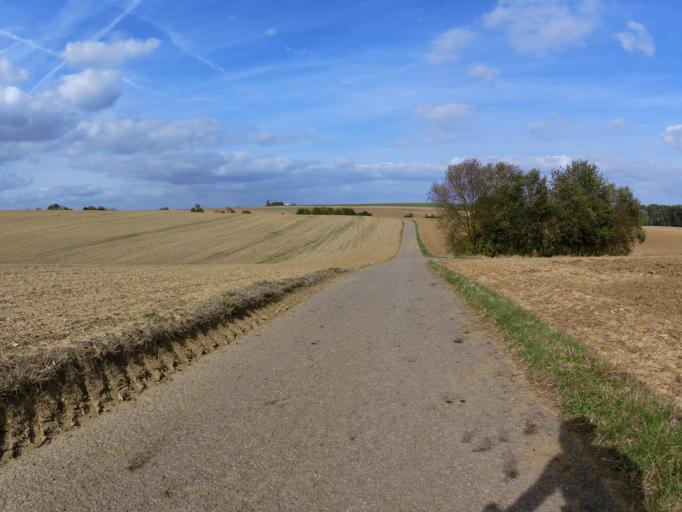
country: DE
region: Bavaria
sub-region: Regierungsbezirk Unterfranken
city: Reichenberg
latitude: 49.7008
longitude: 9.9455
